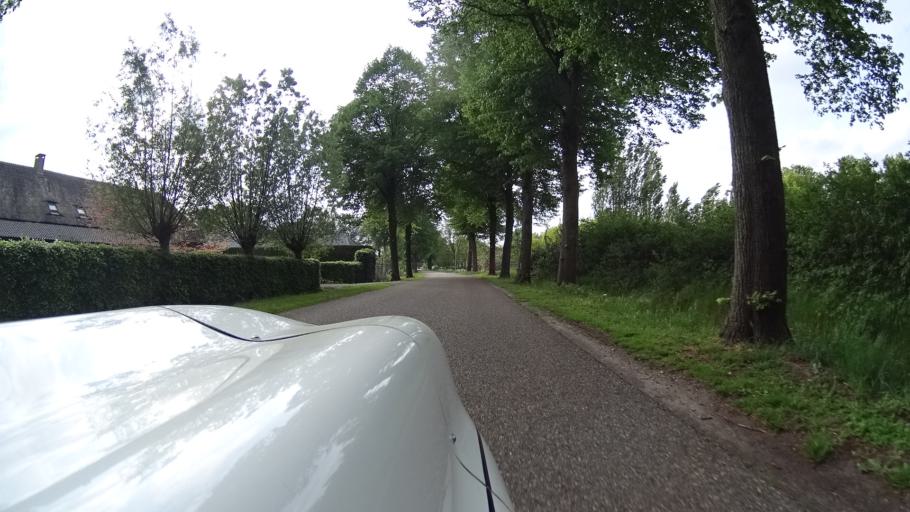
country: NL
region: North Brabant
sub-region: Gemeente Uden
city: Volkel
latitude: 51.6338
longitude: 5.6715
